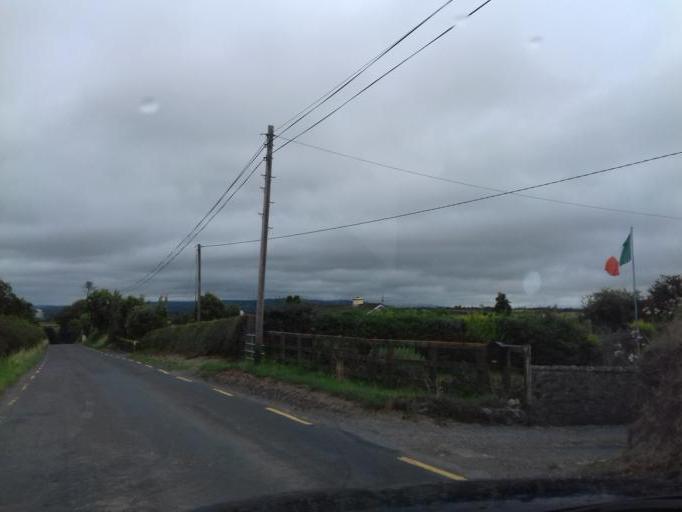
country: IE
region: Leinster
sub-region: County Carlow
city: Bagenalstown
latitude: 52.6212
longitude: -7.0389
